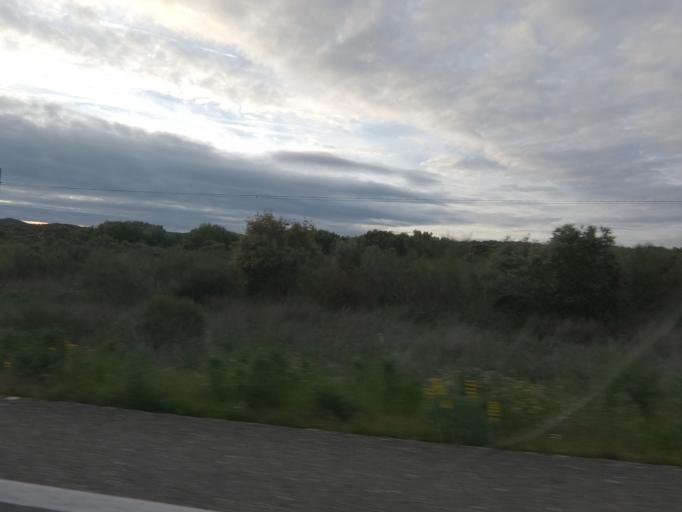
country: ES
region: Extremadura
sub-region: Provincia de Badajoz
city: La Roca de la Sierra
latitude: 39.1197
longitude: -6.6766
